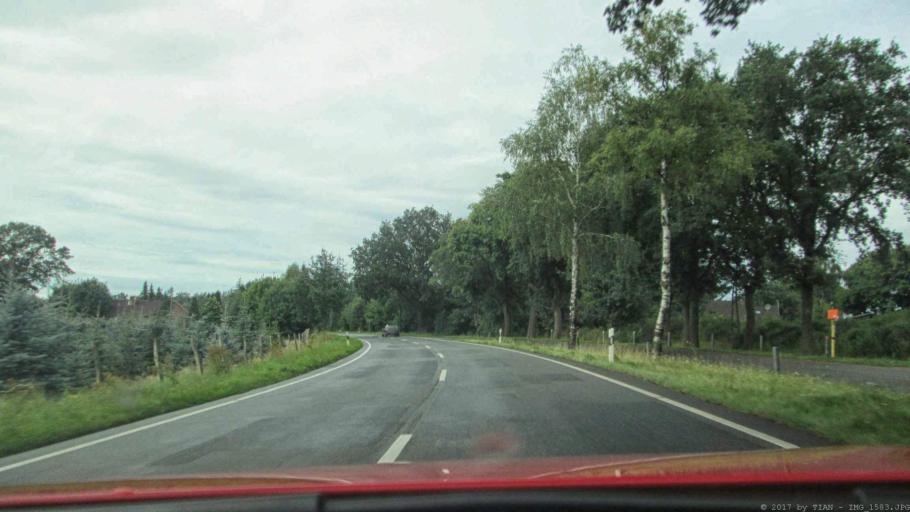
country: DE
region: Lower Saxony
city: Wieren
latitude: 52.8984
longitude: 10.6494
